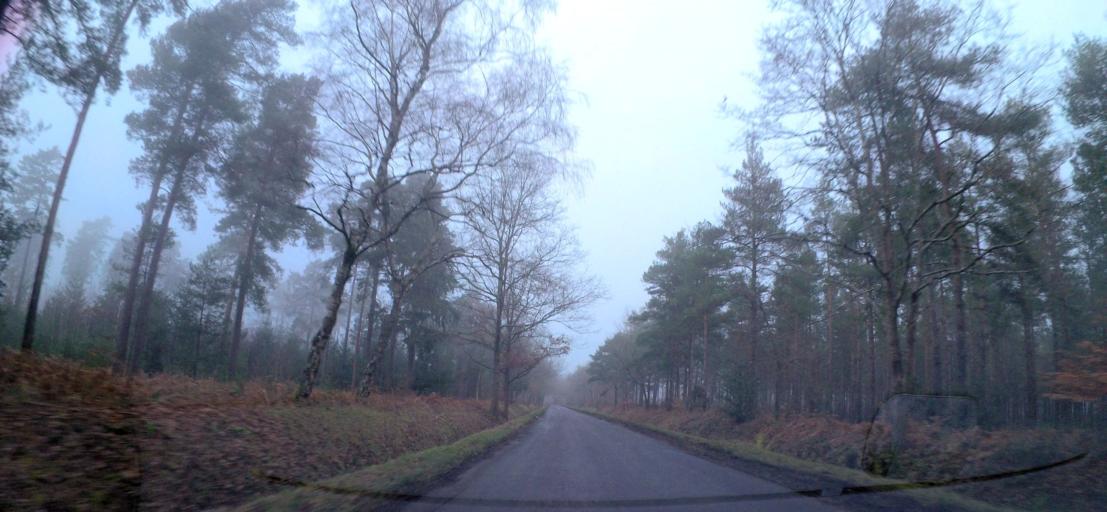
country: GB
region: England
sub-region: West Berkshire
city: Theale
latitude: 51.3910
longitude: -1.0880
